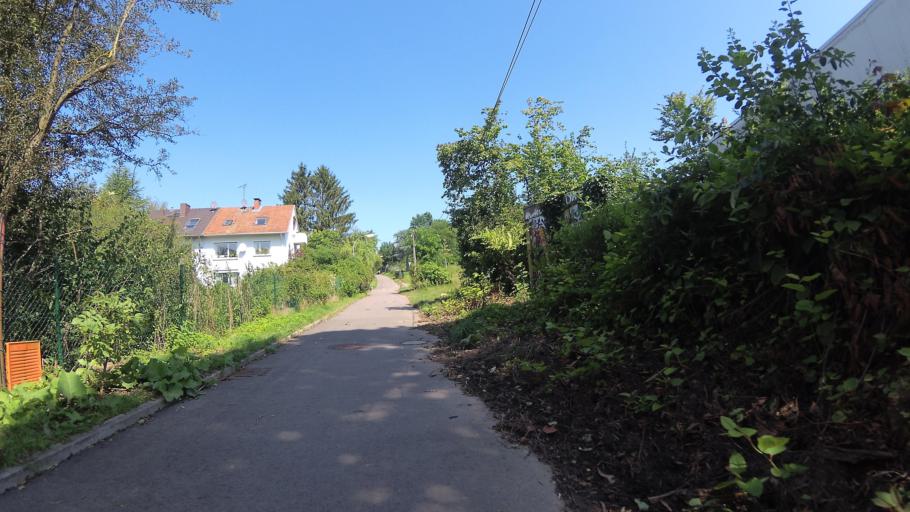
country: DE
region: Saarland
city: Saarbrucken
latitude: 49.2199
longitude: 6.9784
